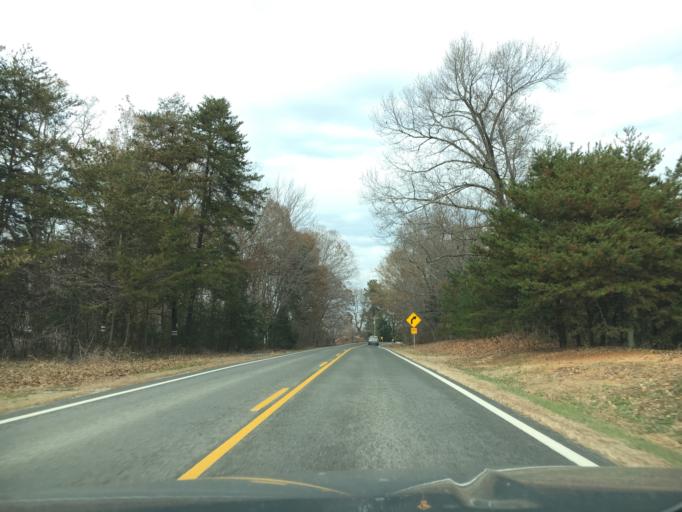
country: US
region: Virginia
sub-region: Prince Edward County
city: Farmville
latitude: 37.3934
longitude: -78.3722
